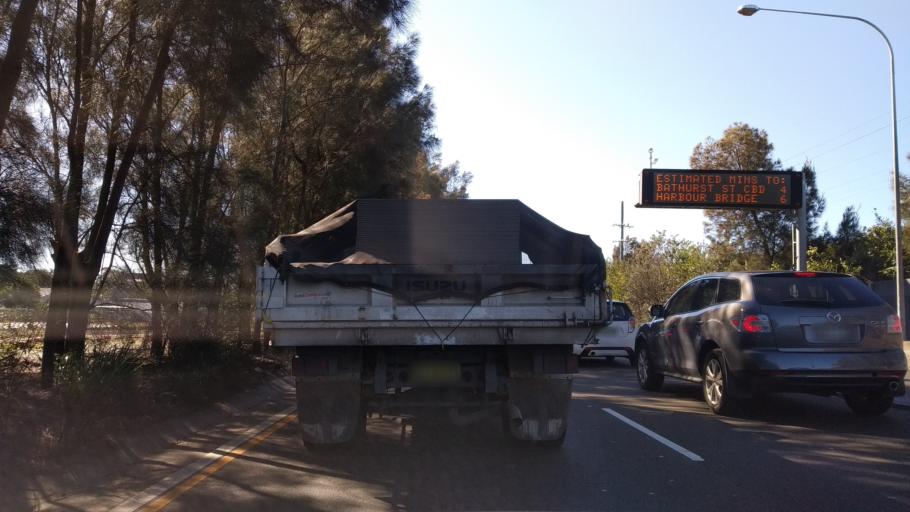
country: AU
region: New South Wales
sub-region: Leichhardt
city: Lilyfield
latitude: -33.8728
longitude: 151.1697
